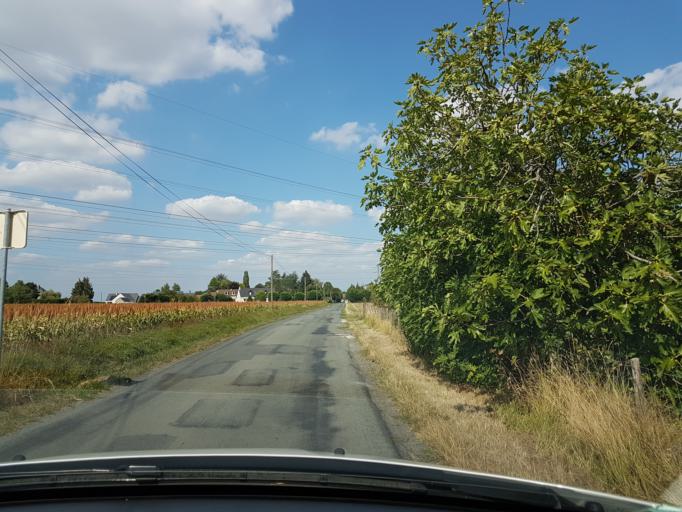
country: FR
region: Centre
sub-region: Departement d'Indre-et-Loire
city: Larcay
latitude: 47.3568
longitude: 0.7800
